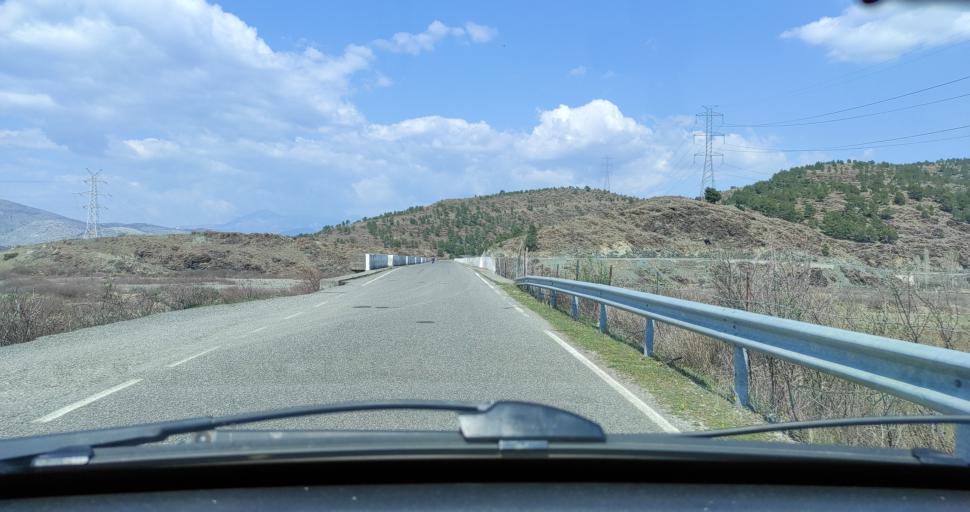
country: AL
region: Shkoder
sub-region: Rrethi i Shkodres
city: Hajmel
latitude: 41.9770
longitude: 19.6451
